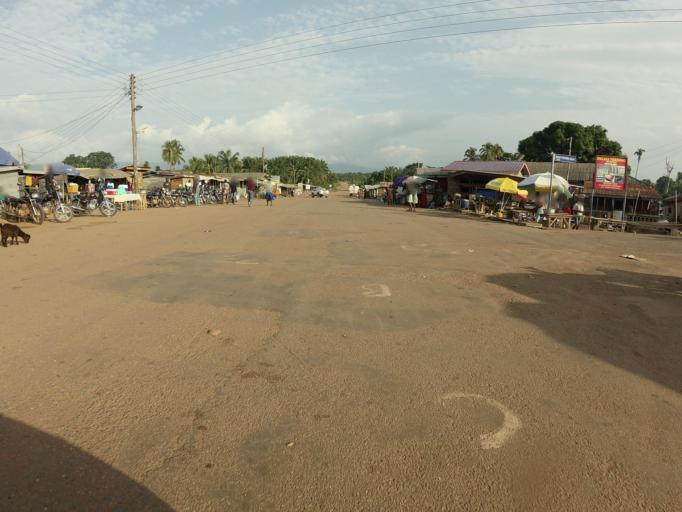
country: GH
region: Volta
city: Kpandu
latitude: 6.9974
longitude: 0.4386
